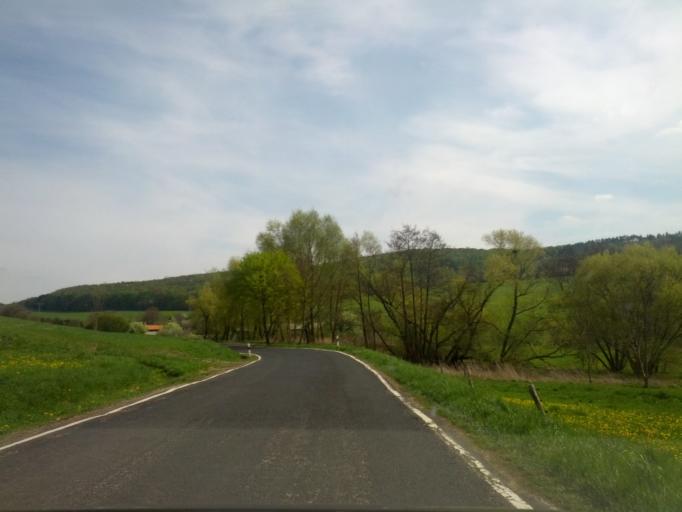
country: DE
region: Thuringia
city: Seebach
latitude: 50.9765
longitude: 10.4444
